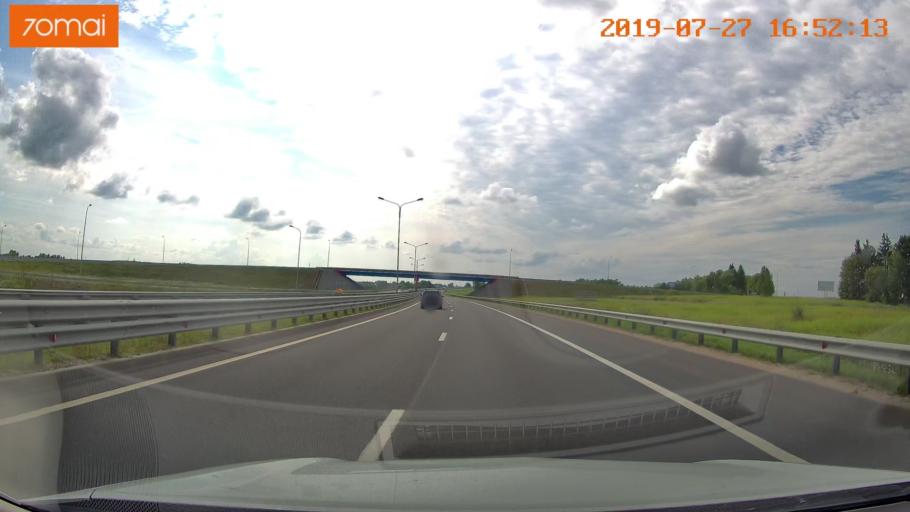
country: RU
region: Kaliningrad
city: Gvardeysk
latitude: 54.6840
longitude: 20.8664
